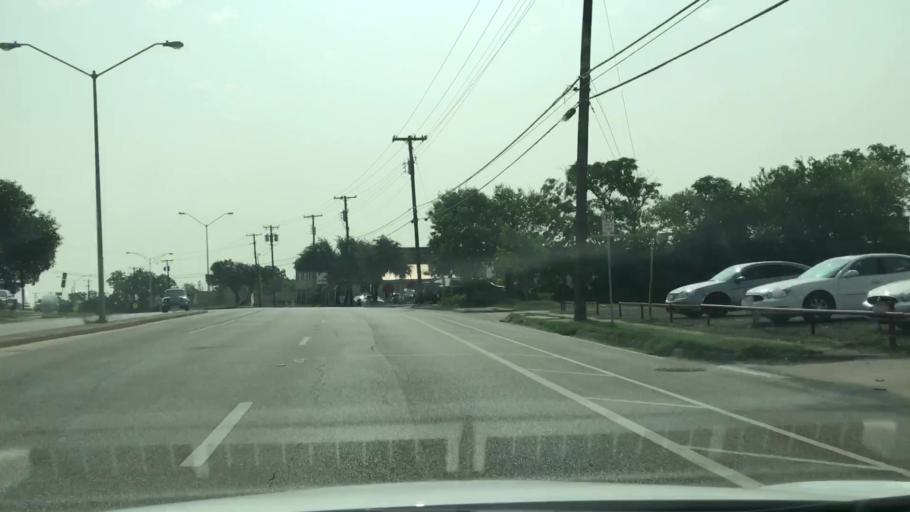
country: US
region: Texas
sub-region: Dallas County
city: Dallas
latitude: 32.7654
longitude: -96.8464
